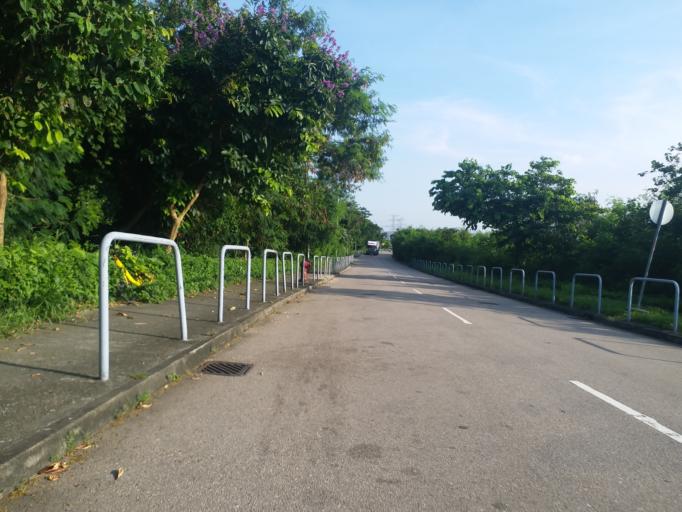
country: HK
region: Yuen Long
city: Yuen Long Kau Hui
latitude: 22.4757
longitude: 114.0517
